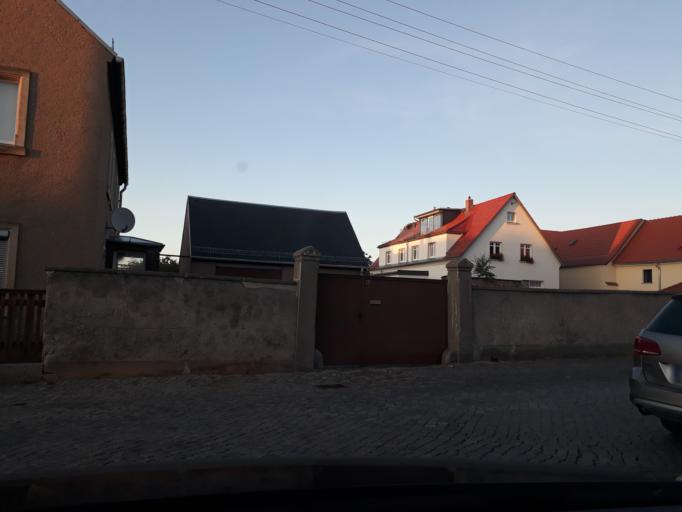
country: DE
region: Saxony
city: Radebeul
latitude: 51.1190
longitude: 13.6699
